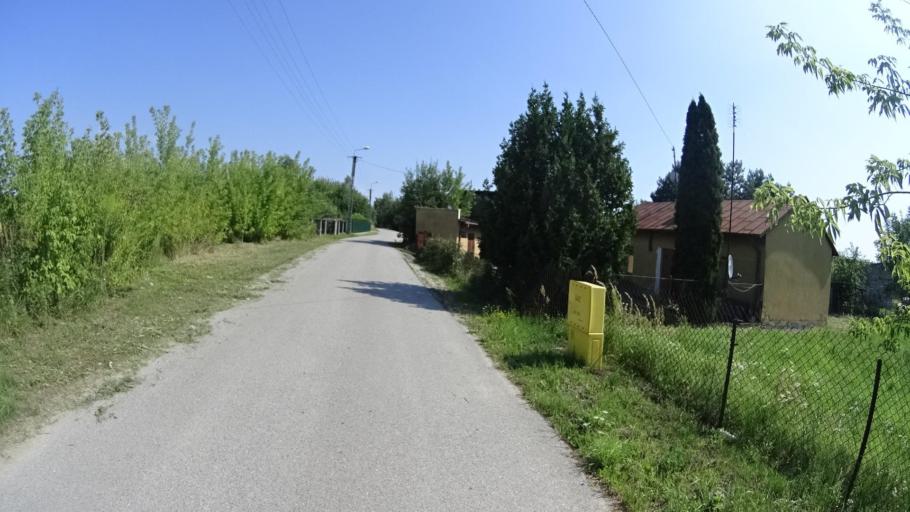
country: PL
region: Masovian Voivodeship
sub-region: Powiat grojecki
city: Grojec
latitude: 51.8523
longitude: 20.8626
